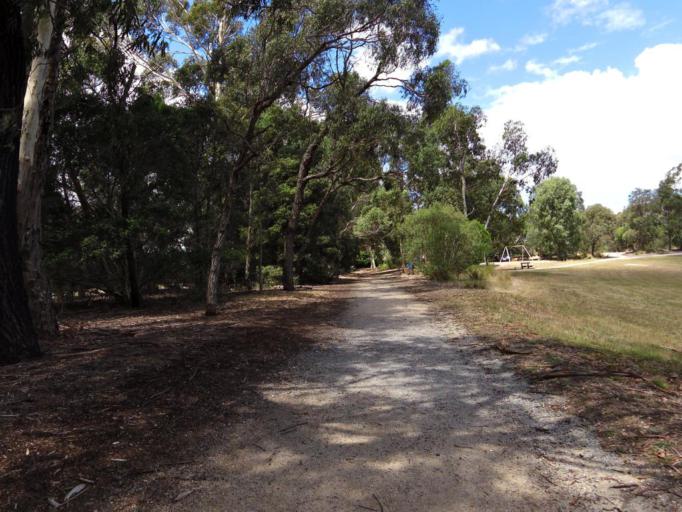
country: AU
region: Victoria
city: Burwood East
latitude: -37.8409
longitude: 145.1384
